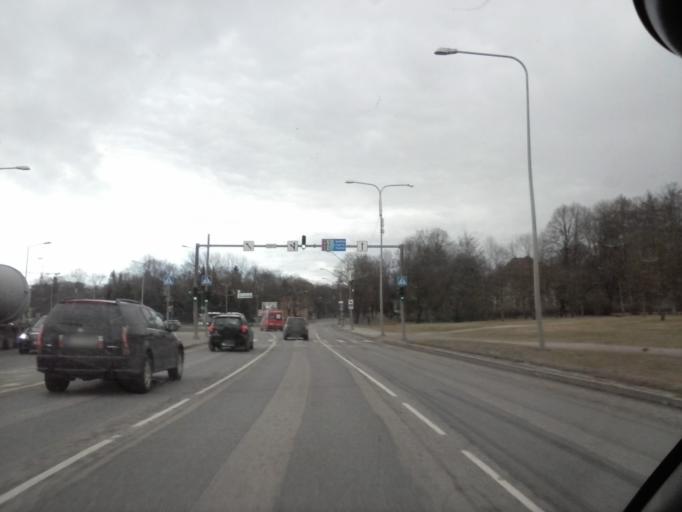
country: EE
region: Harju
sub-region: Tallinna linn
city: Tallinn
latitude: 59.4428
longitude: 24.7937
